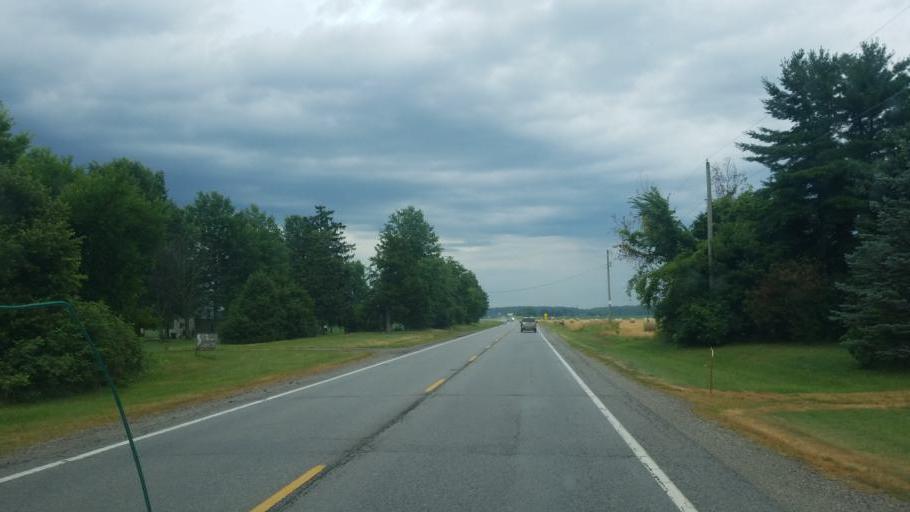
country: US
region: Ohio
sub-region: Williams County
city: Edgerton
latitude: 41.4445
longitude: -84.6757
